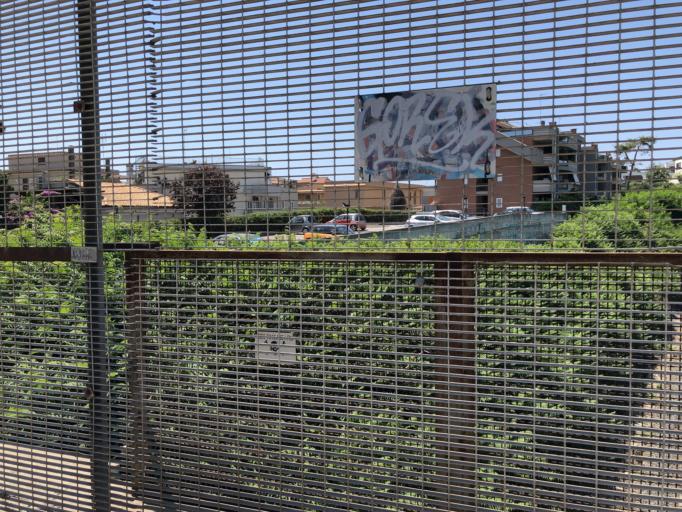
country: IT
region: Latium
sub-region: Citta metropolitana di Roma Capitale
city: Nettuno
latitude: 41.4578
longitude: 12.6511
